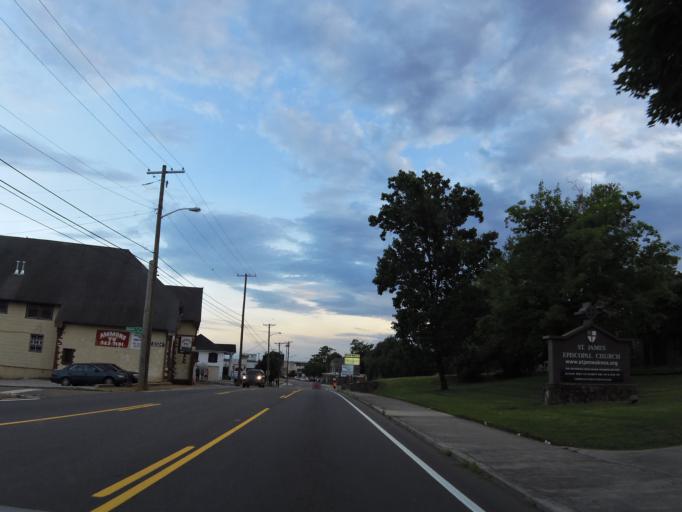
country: US
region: Tennessee
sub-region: Knox County
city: Knoxville
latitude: 35.9827
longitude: -83.9228
